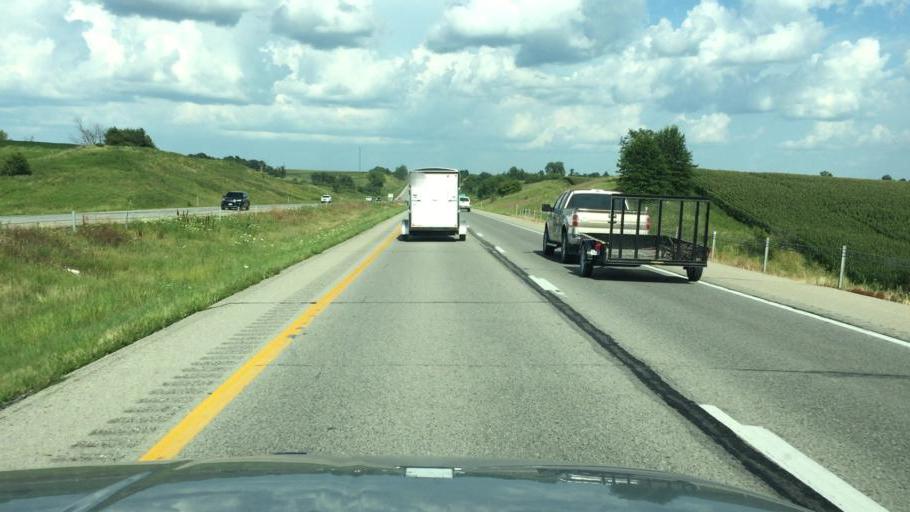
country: US
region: Iowa
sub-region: Poweshiek County
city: Grinnell
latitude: 41.6951
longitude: -92.8299
